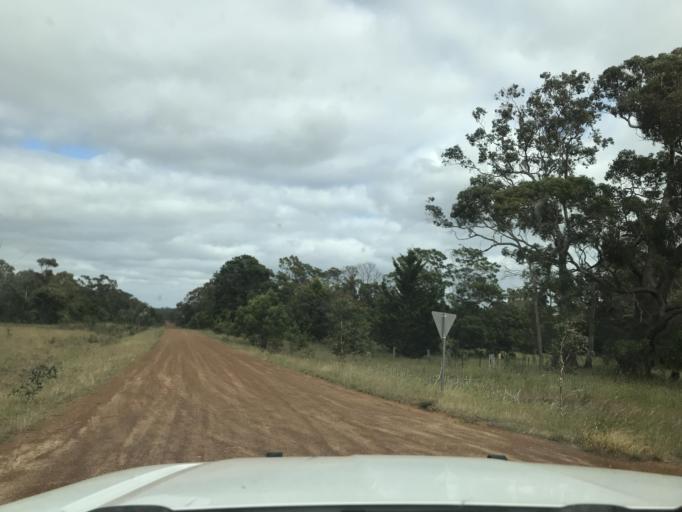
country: AU
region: South Australia
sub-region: Wattle Range
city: Penola
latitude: -37.3344
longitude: 141.4231
